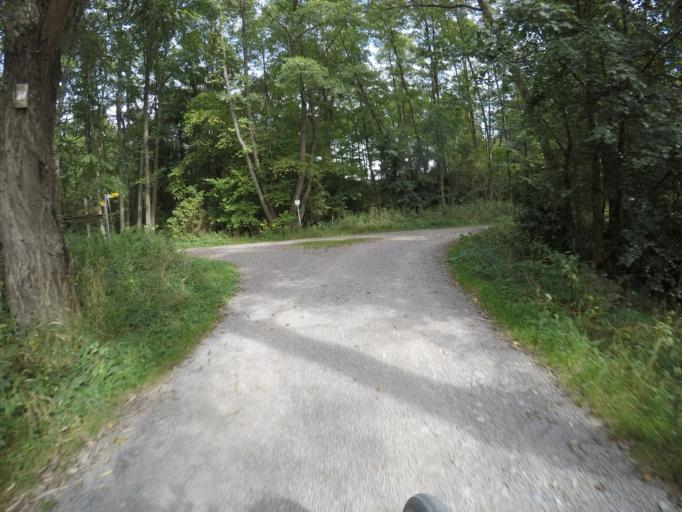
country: DE
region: Baden-Wuerttemberg
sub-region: Karlsruhe Region
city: Illingen
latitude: 48.9702
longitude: 8.8865
